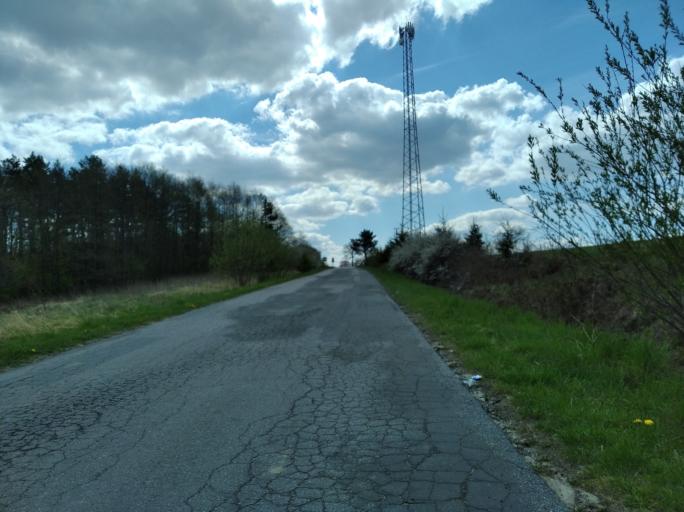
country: PL
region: Subcarpathian Voivodeship
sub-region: Powiat brzozowski
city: Wesola
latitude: 49.7671
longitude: 22.1260
